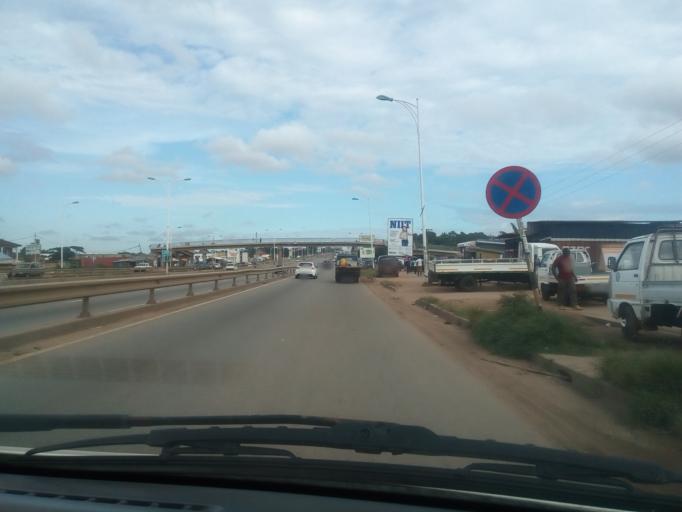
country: GH
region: Greater Accra
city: Dome
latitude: 5.6504
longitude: -0.2545
